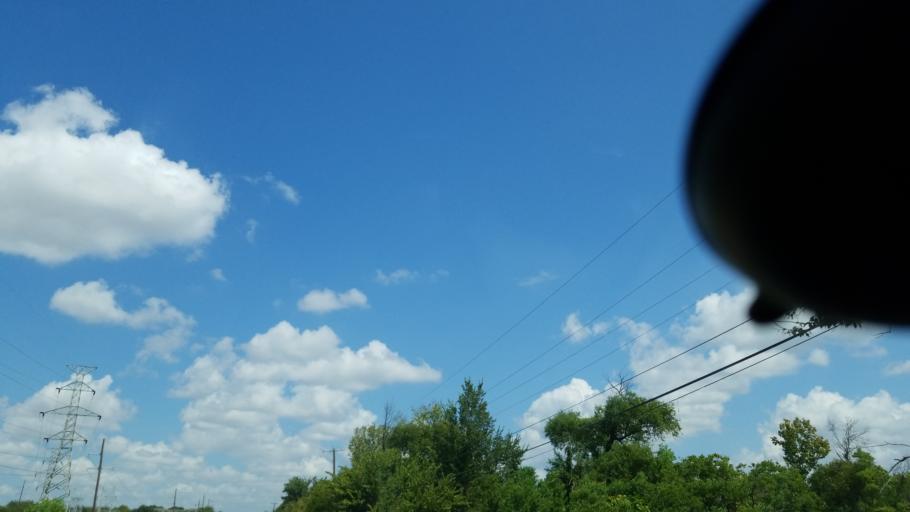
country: US
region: Texas
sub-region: Dallas County
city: Grand Prairie
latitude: 32.7281
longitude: -96.9858
